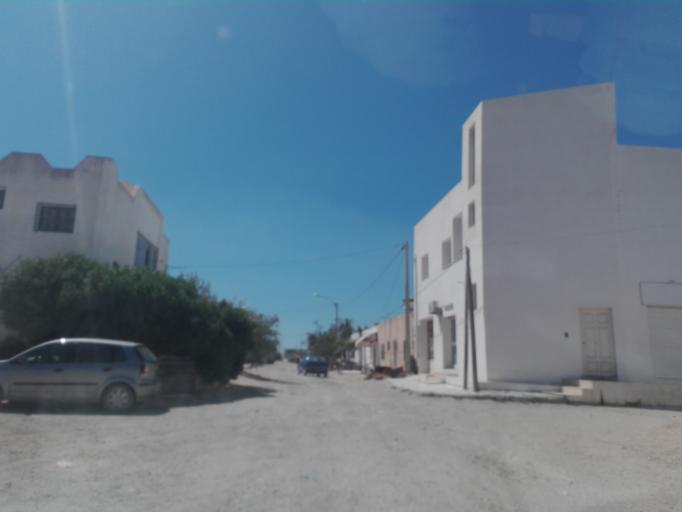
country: TN
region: Safaqis
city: Jabinyanah
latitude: 34.7432
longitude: 11.2972
